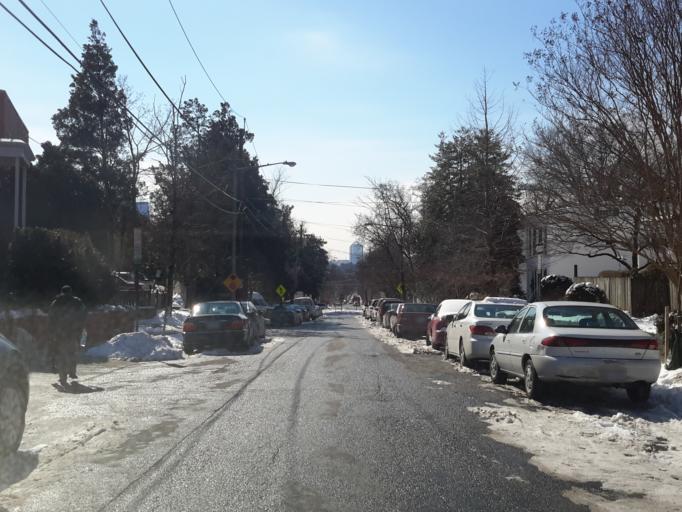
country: US
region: Maryland
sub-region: Montgomery County
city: Friendship Village
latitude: 38.9211
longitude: -77.0731
